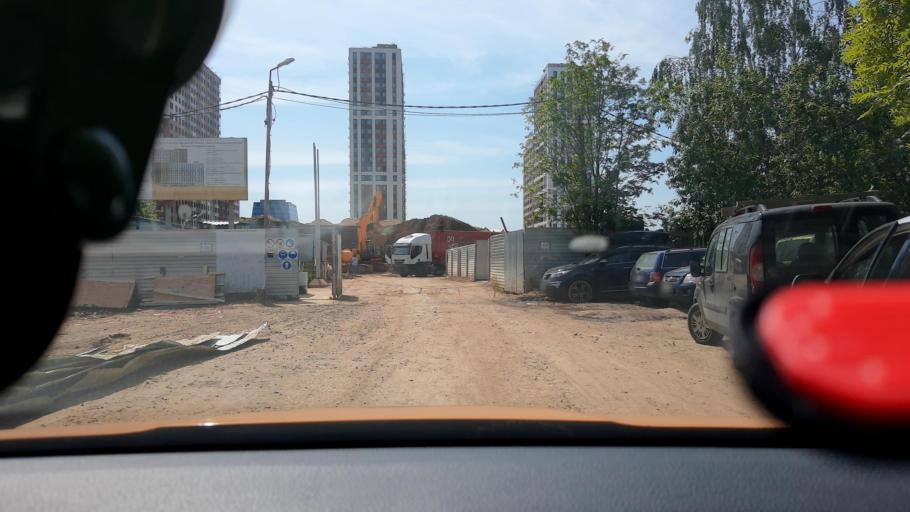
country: RU
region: Moskovskaya
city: Novoivanovskoye
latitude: 55.7034
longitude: 37.3582
